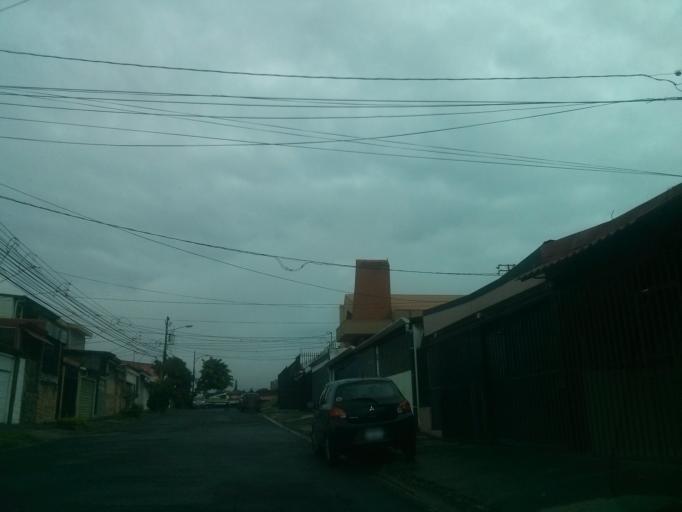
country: CR
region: San Jose
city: Curridabat
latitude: 9.9178
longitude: -84.0421
